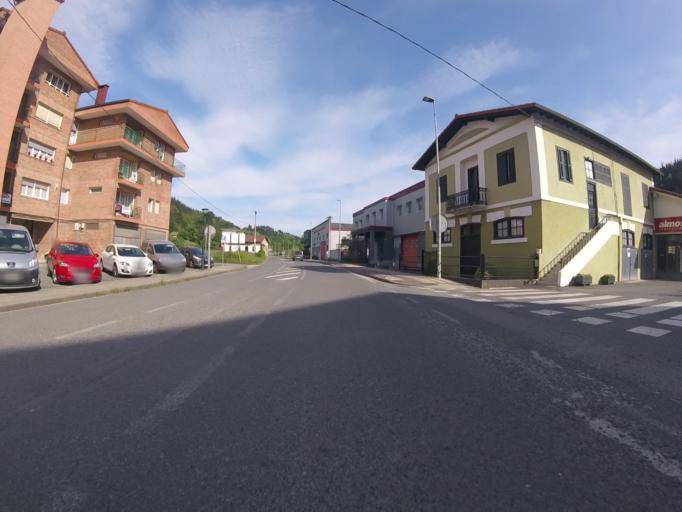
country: ES
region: Basque Country
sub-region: Provincia de Guipuzcoa
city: Ormaiztegui
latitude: 43.0439
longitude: -2.2567
